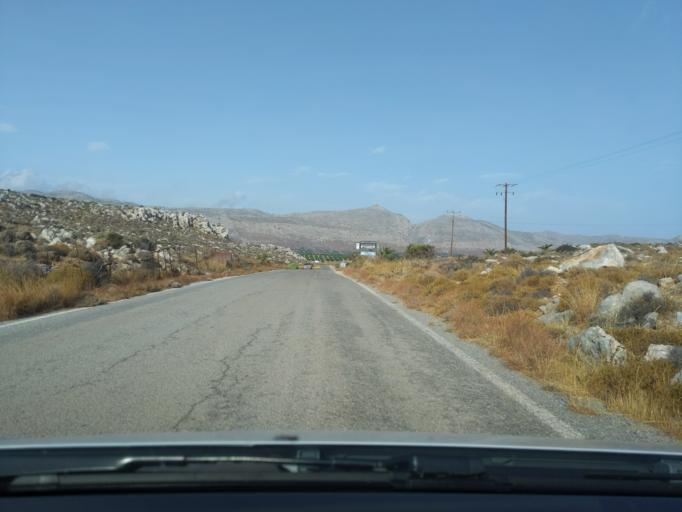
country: GR
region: Crete
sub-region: Nomos Lasithiou
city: Palekastro
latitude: 35.0854
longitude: 26.2523
